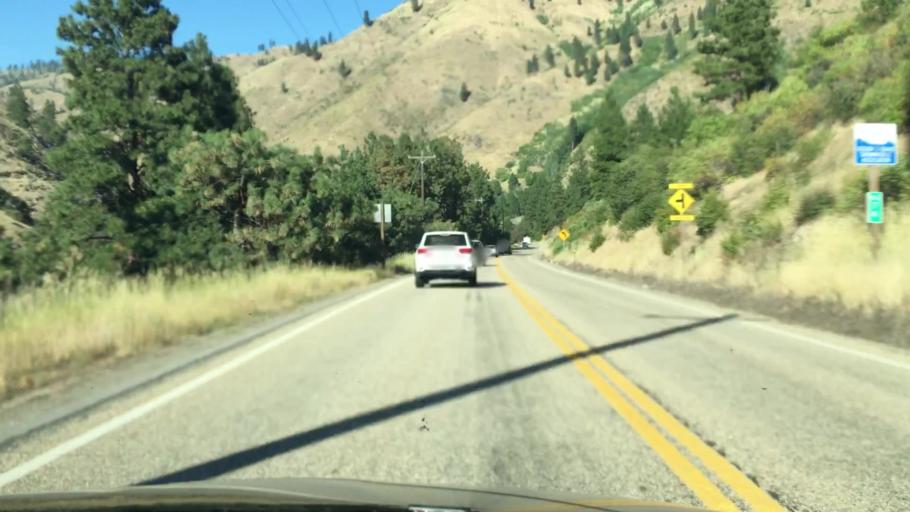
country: US
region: Idaho
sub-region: Boise County
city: Idaho City
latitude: 44.0248
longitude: -116.1427
